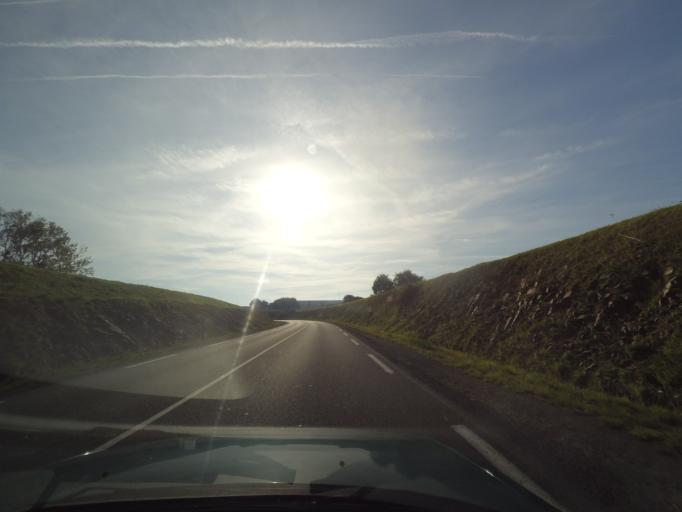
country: FR
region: Pays de la Loire
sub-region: Departement de la Vendee
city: Montaigu
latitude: 46.9642
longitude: -1.3028
